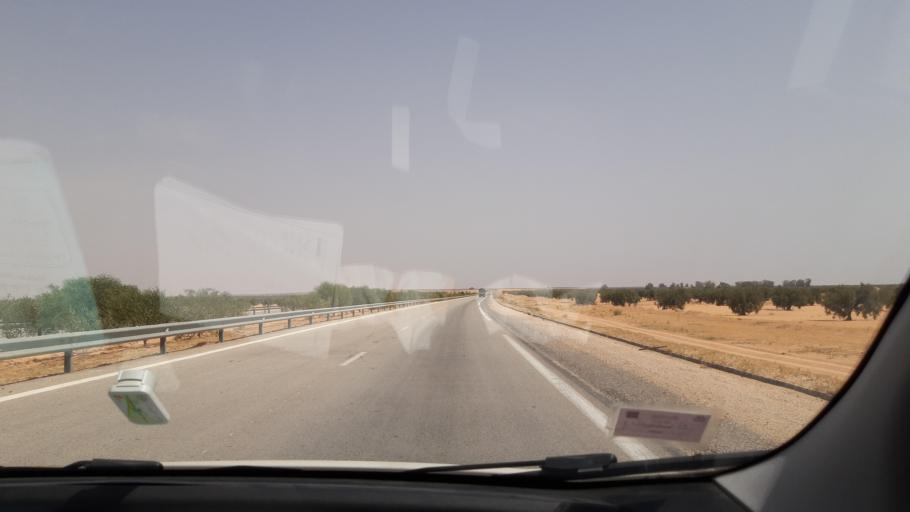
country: TN
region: Safaqis
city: Bi'r `Ali Bin Khalifah
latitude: 34.5311
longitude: 10.1003
